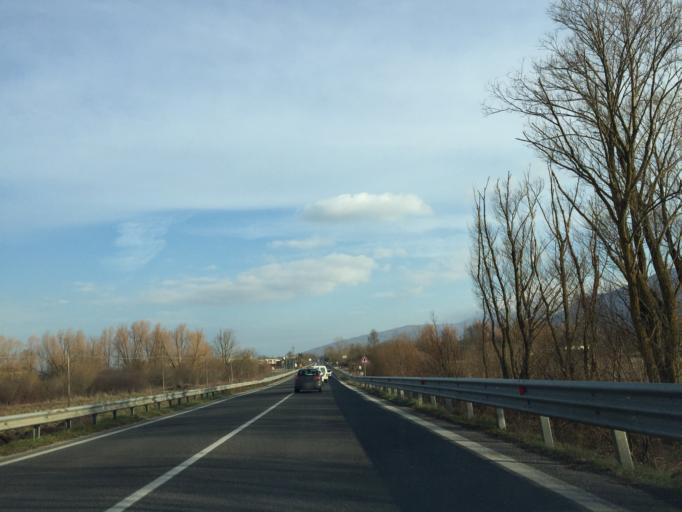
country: IT
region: Molise
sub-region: Provincia di Campobasso
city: Bojano
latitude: 41.4834
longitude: 14.4937
